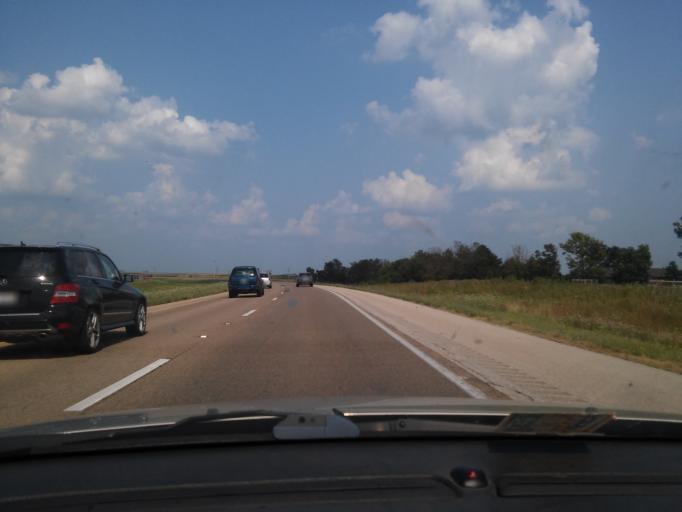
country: US
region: Illinois
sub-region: McLean County
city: Lexington
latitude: 40.6597
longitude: -88.7790
